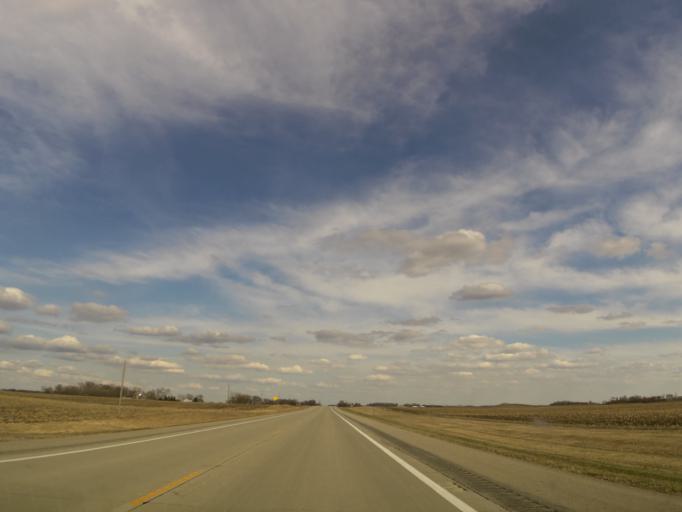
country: US
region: Minnesota
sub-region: Lac qui Parle County
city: Dawson
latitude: 44.9356
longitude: -95.9569
